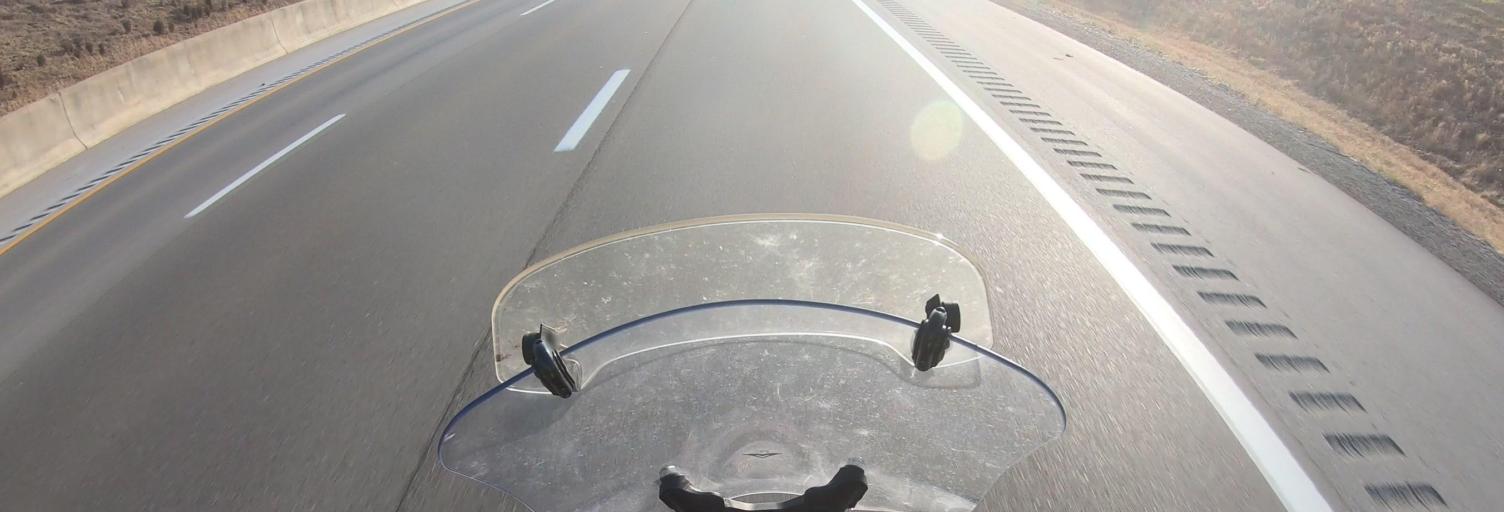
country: US
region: Kentucky
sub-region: Grant County
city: Williamstown
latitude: 38.6038
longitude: -84.5788
